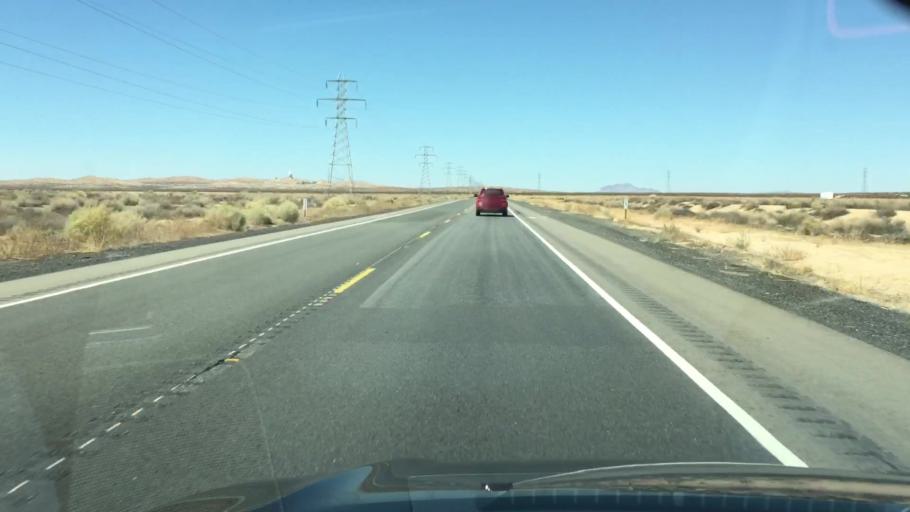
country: US
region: California
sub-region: Kern County
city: Boron
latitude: 35.0280
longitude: -117.5515
